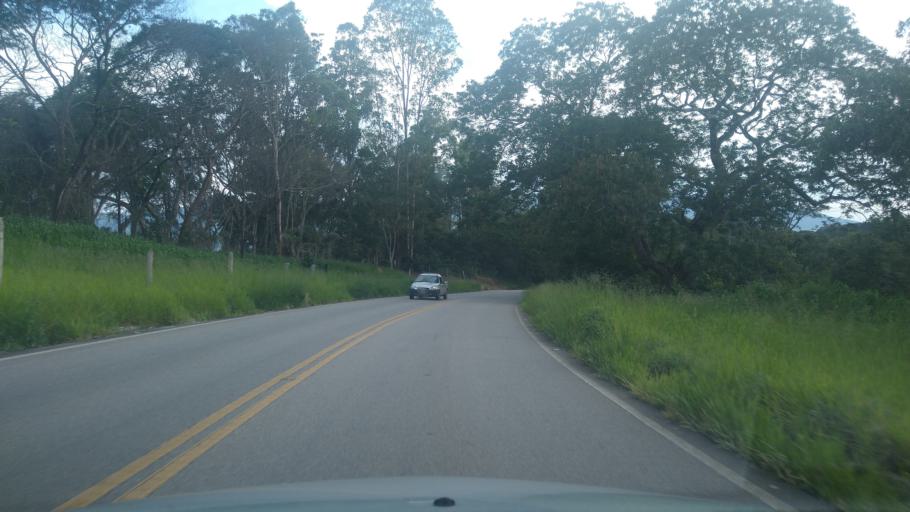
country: BR
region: Minas Gerais
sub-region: Extrema
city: Extrema
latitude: -22.7825
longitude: -46.3210
